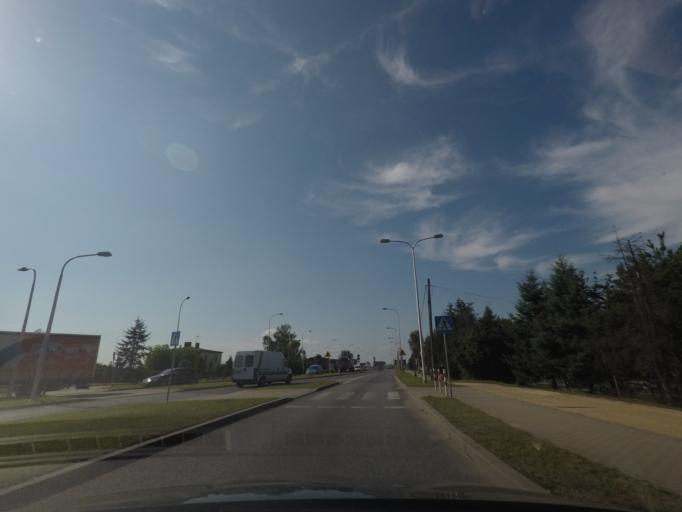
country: PL
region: Silesian Voivodeship
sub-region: Zory
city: Zory
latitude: 50.0617
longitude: 18.6634
